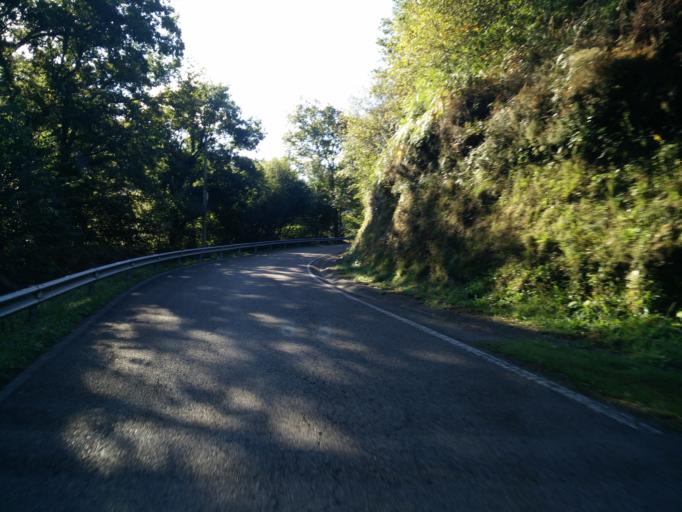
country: ES
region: Cantabria
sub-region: Provincia de Cantabria
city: San Pedro del Romeral
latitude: 43.1457
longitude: -3.8188
